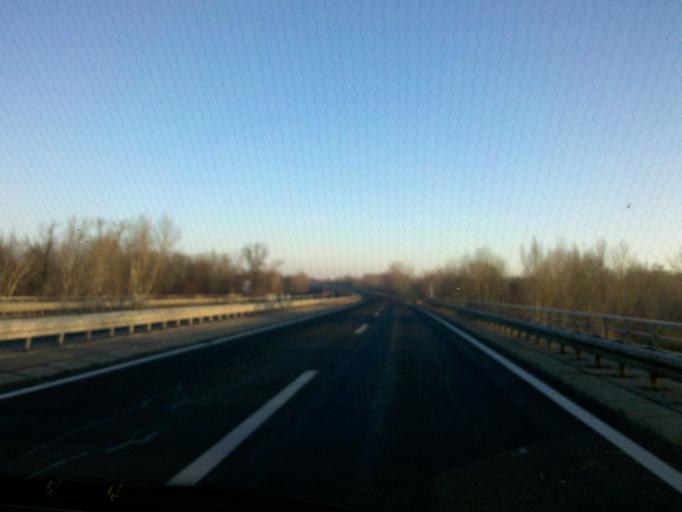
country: HR
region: Medimurska
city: Orehovica
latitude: 46.2987
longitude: 16.4994
